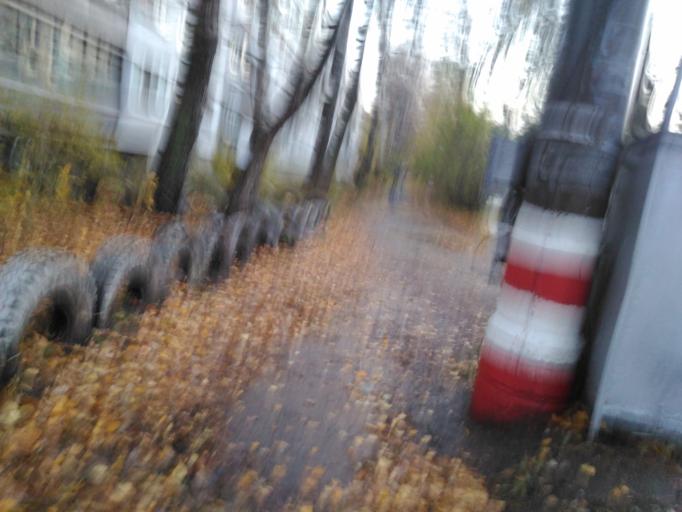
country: RU
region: Ulyanovsk
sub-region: Ulyanovskiy Rayon
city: Ulyanovsk
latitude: 54.3238
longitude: 48.3855
